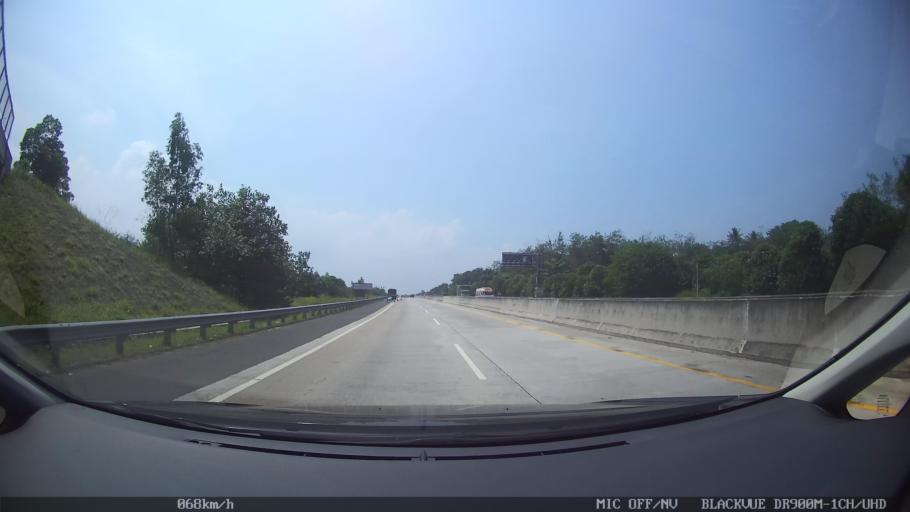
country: ID
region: Lampung
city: Kedaton
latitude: -5.3774
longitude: 105.3300
